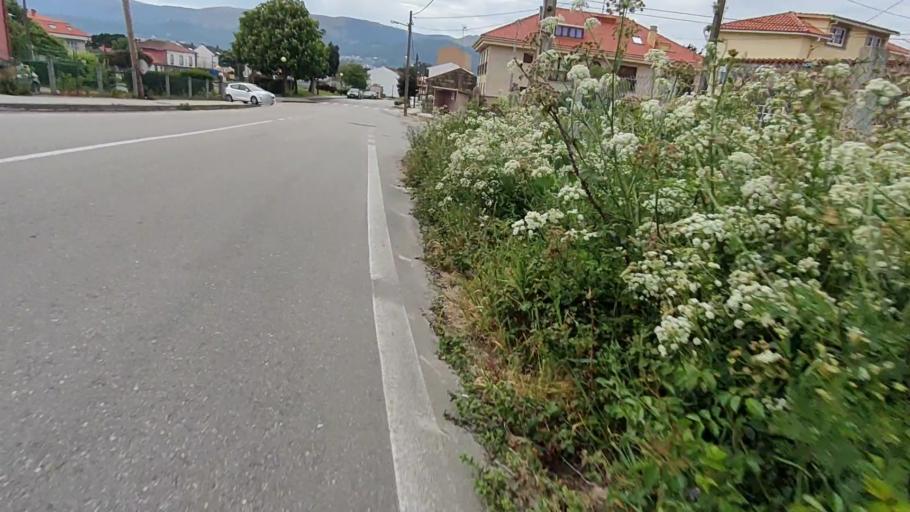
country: ES
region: Galicia
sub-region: Provincia da Coruna
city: Boiro
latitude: 42.6351
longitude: -8.8727
